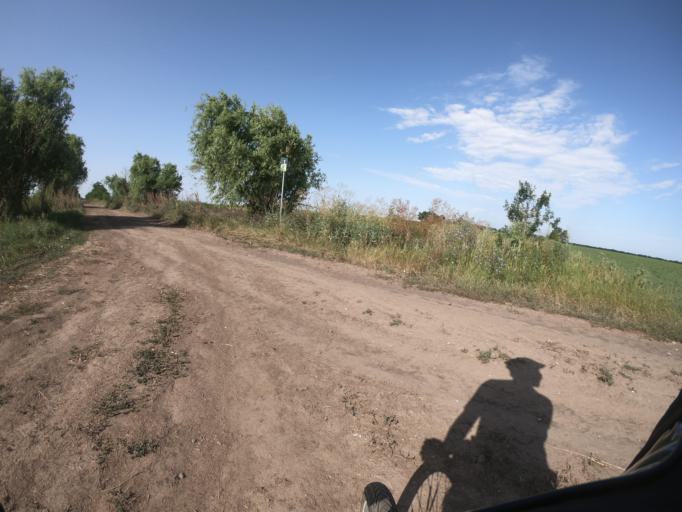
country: HU
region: Hajdu-Bihar
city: Egyek
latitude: 47.5980
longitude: 20.9697
